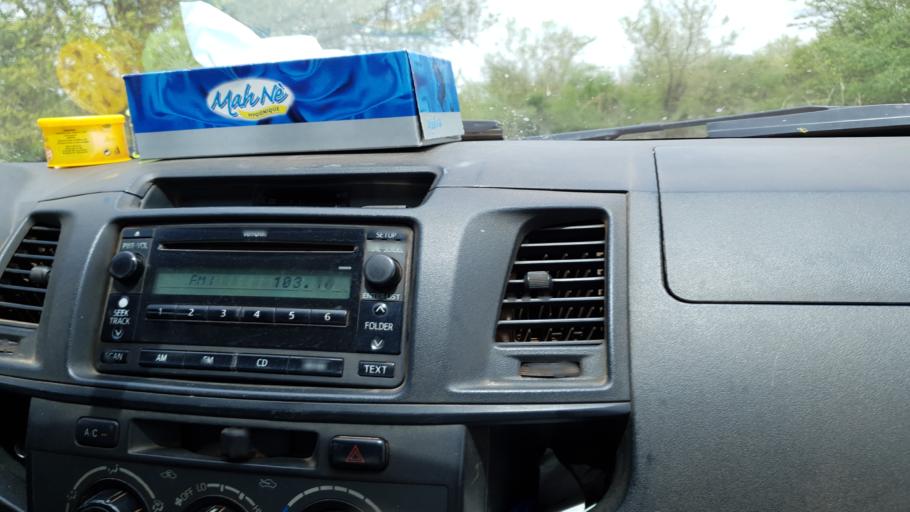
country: ML
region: Segou
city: Baroueli
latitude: 13.3546
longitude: -7.0978
